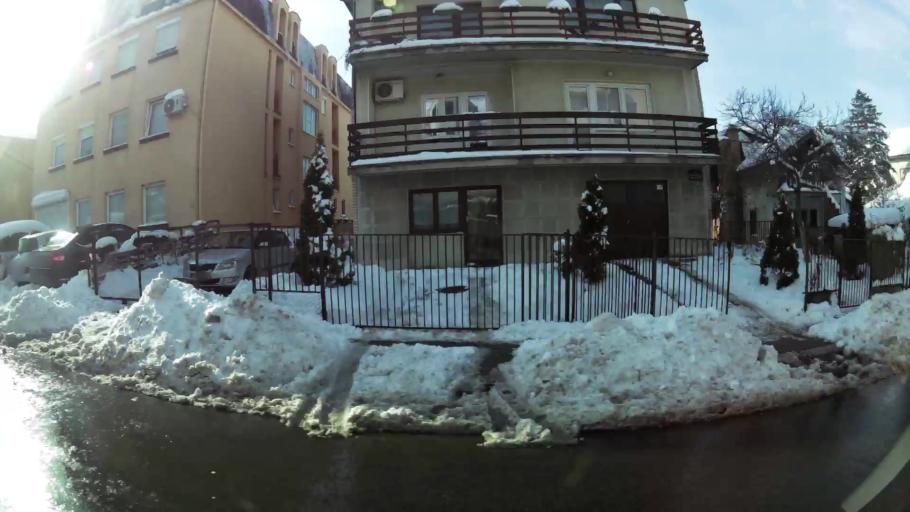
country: RS
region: Central Serbia
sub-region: Belgrade
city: Zvezdara
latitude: 44.7945
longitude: 20.5338
